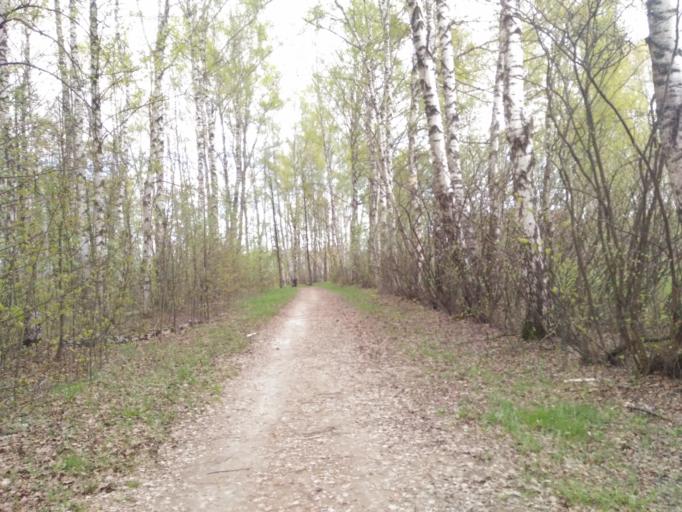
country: RU
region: Moskovskaya
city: Nakhabino
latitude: 55.8443
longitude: 37.1685
